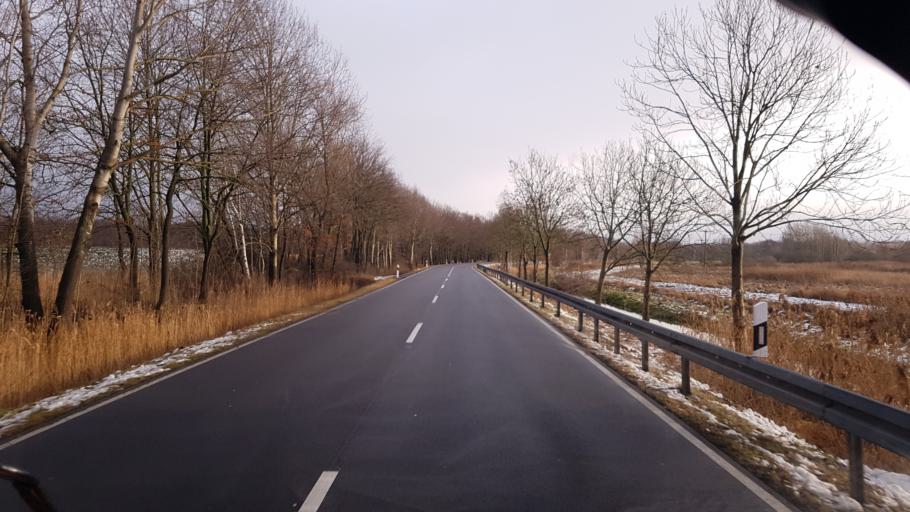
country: DE
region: Brandenburg
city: Heinersbruck
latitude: 51.8184
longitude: 14.5921
